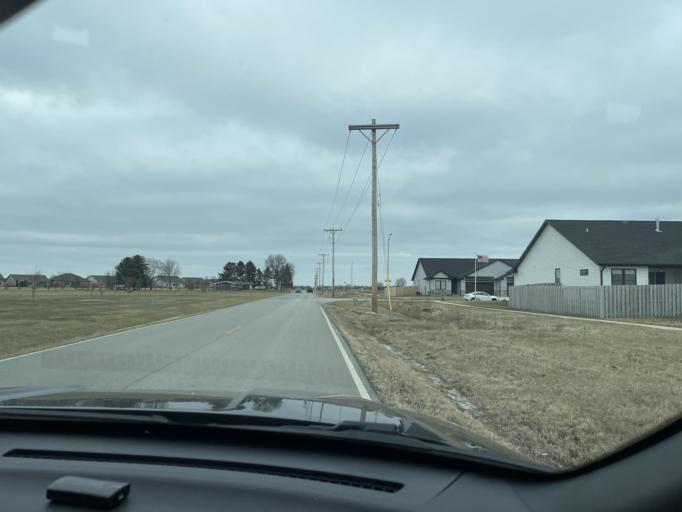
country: US
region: Illinois
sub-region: Sangamon County
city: Jerome
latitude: 39.7617
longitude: -89.7532
